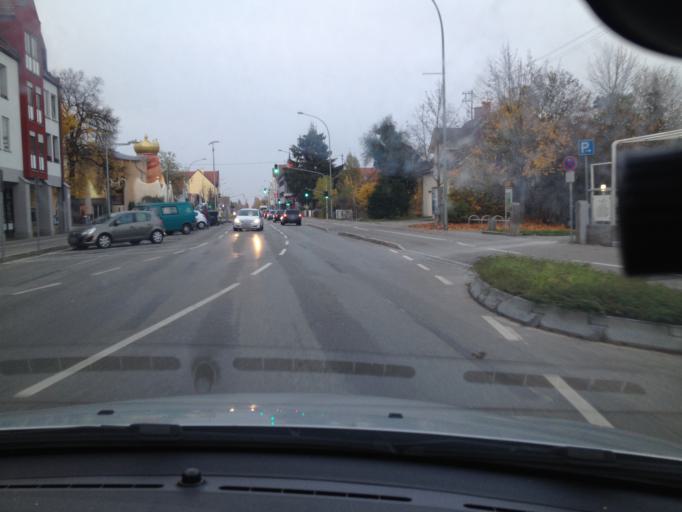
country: DE
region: Bavaria
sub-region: Swabia
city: Konigsbrunn
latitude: 48.2687
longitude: 10.8876
